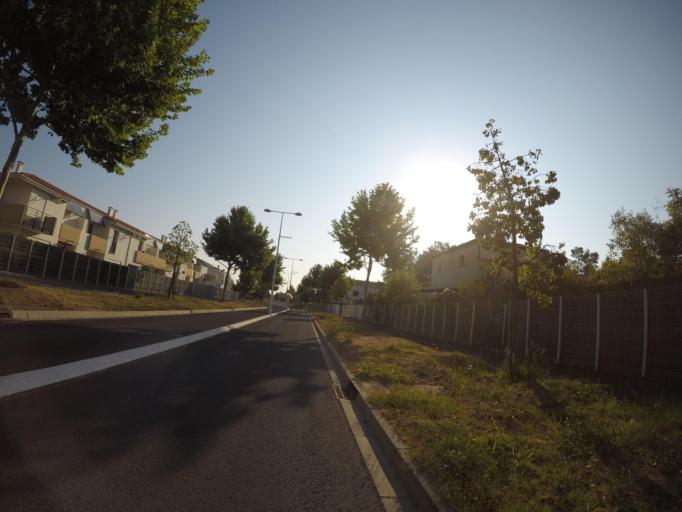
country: FR
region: Languedoc-Roussillon
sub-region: Departement des Pyrenees-Orientales
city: Le Soler
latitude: 42.6783
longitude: 2.8059
